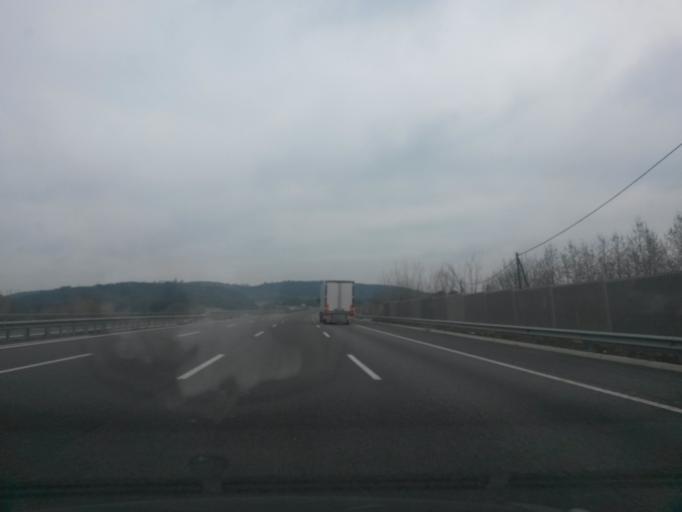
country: ES
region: Catalonia
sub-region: Provincia de Girona
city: Sant Julia de Ramis
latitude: 42.0435
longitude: 2.8567
